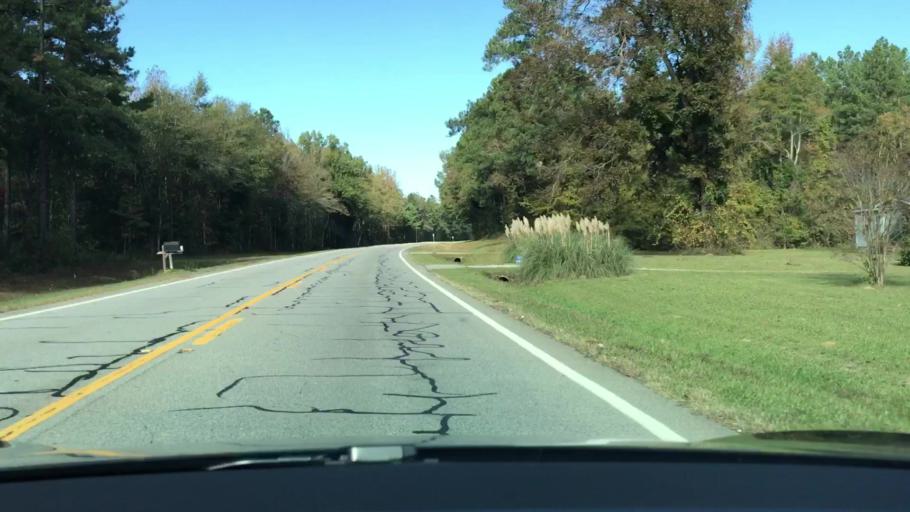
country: US
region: Georgia
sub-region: Warren County
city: Warrenton
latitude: 33.3468
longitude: -82.5820
